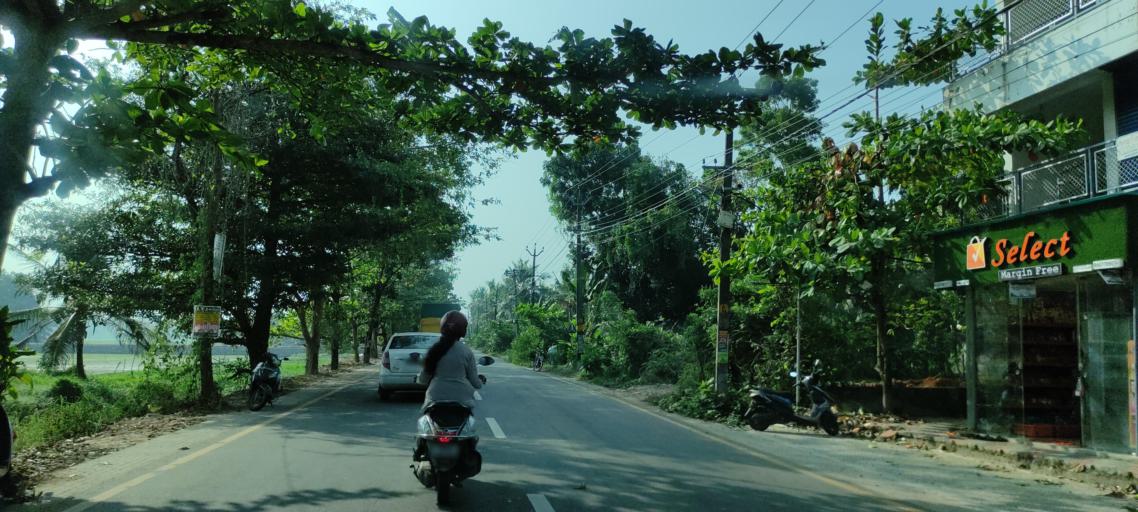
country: IN
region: Kerala
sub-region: Kottayam
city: Changanacheri
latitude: 9.3618
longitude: 76.4617
